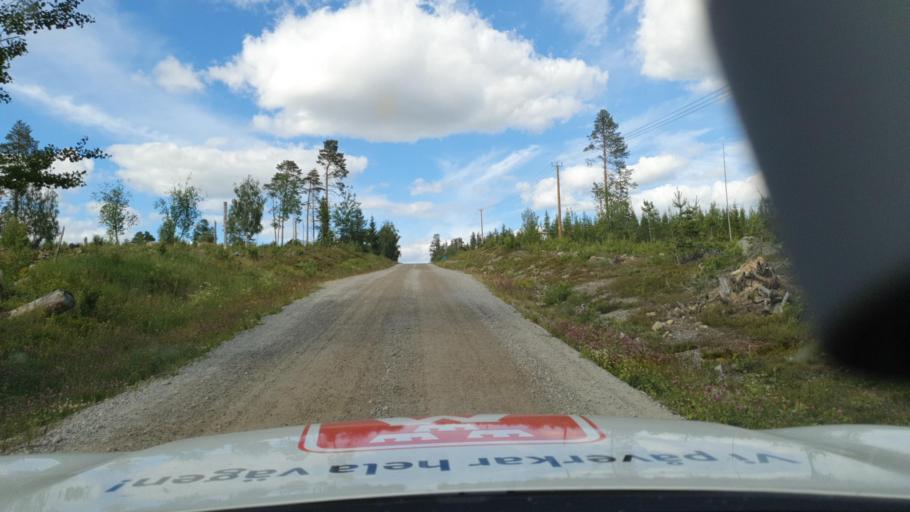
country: SE
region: Vaesterbotten
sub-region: Lycksele Kommun
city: Soderfors
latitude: 64.2865
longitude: 18.1702
